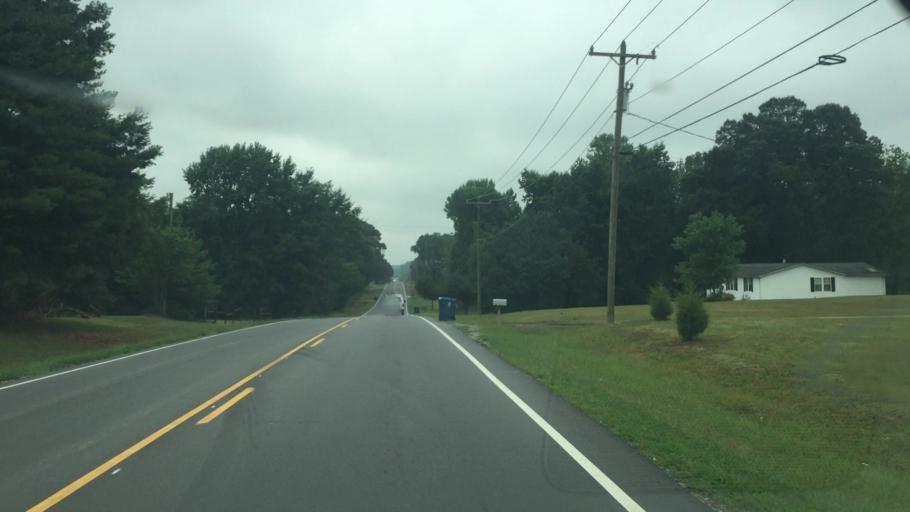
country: US
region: North Carolina
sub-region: Rowan County
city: Enochville
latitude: 35.4399
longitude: -80.7253
